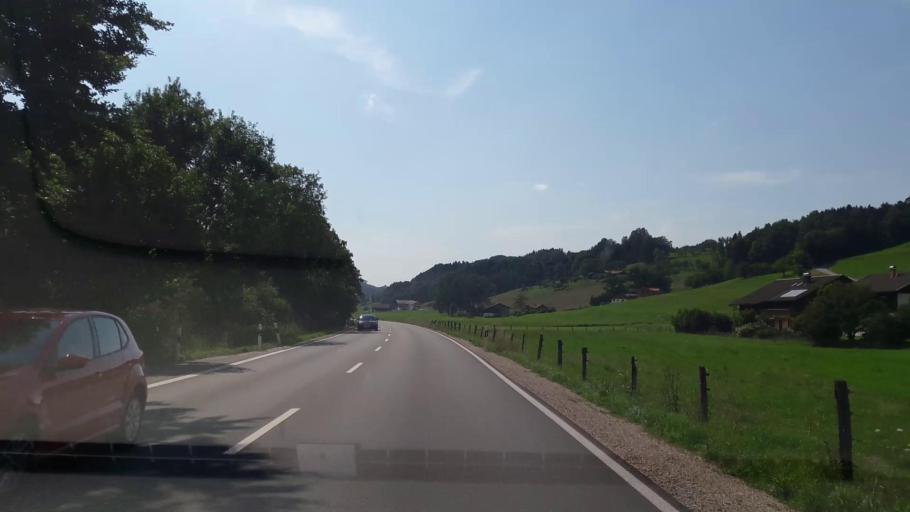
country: DE
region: Bavaria
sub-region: Upper Bavaria
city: Teisendorf
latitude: 47.8572
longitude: 12.7720
